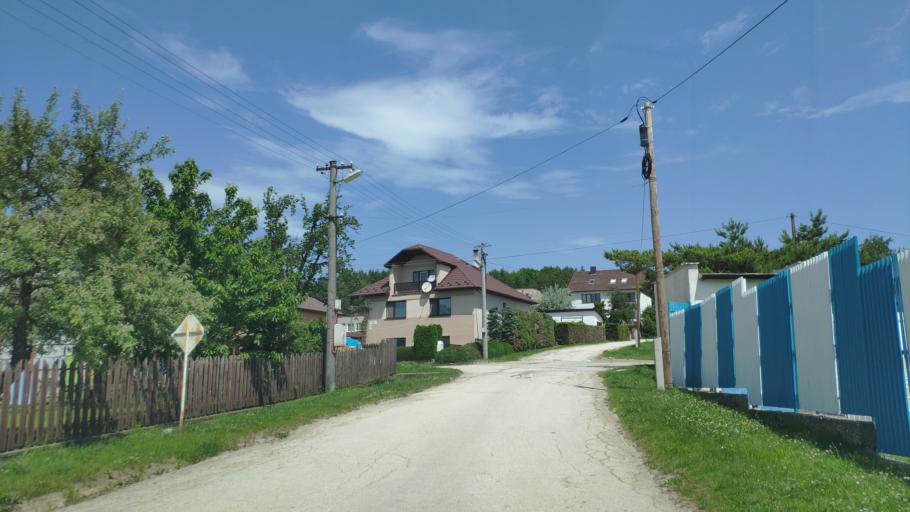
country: SK
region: Kosicky
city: Medzev
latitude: 48.7152
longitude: 20.9803
